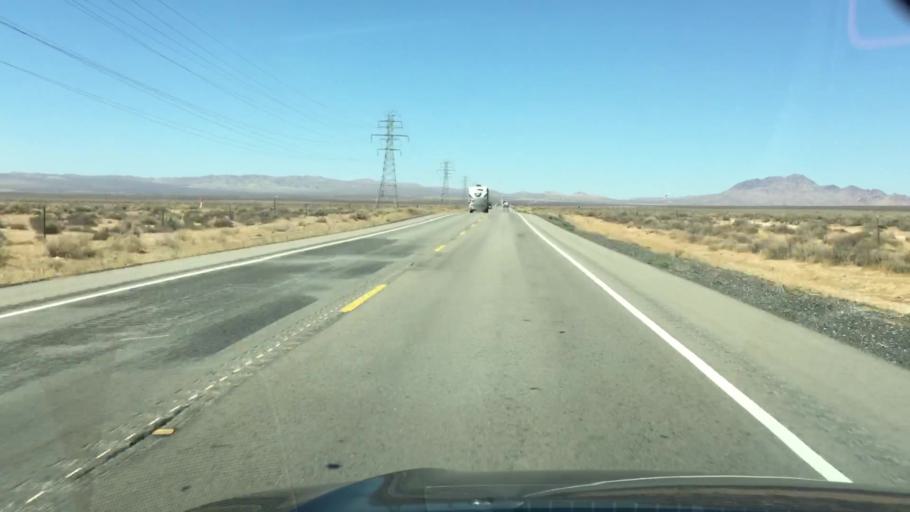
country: US
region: California
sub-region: Kern County
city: Boron
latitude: 35.1914
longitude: -117.5973
